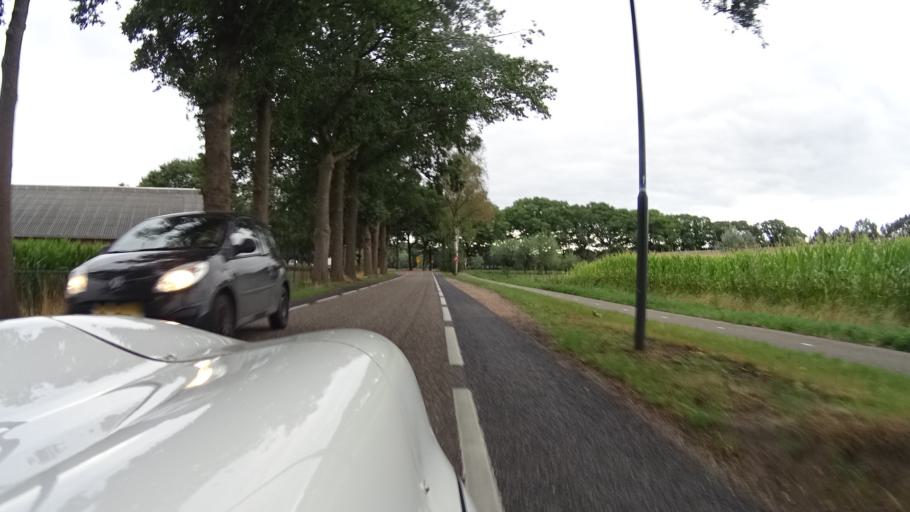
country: NL
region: North Brabant
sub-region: Gemeente Maasdonk
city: Geffen
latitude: 51.6947
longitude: 5.4550
